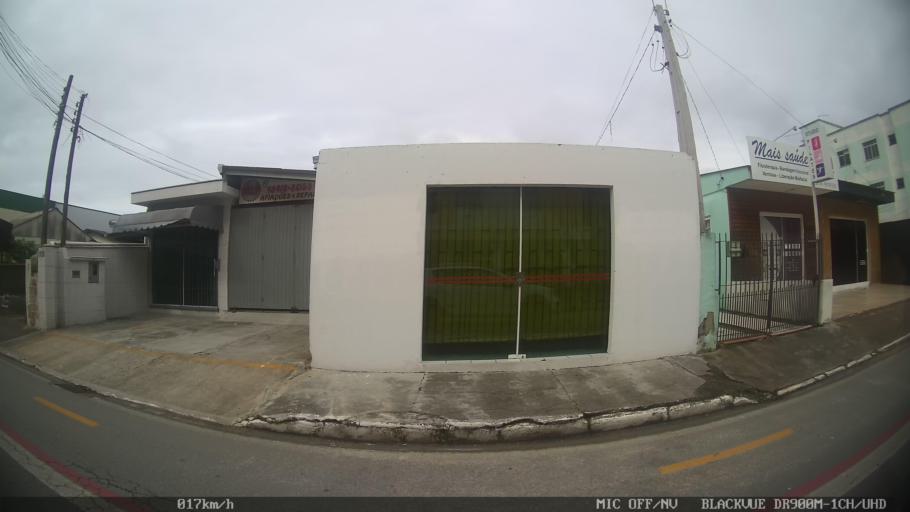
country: BR
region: Santa Catarina
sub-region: Sao Jose
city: Campinas
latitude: -27.5595
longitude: -48.6316
